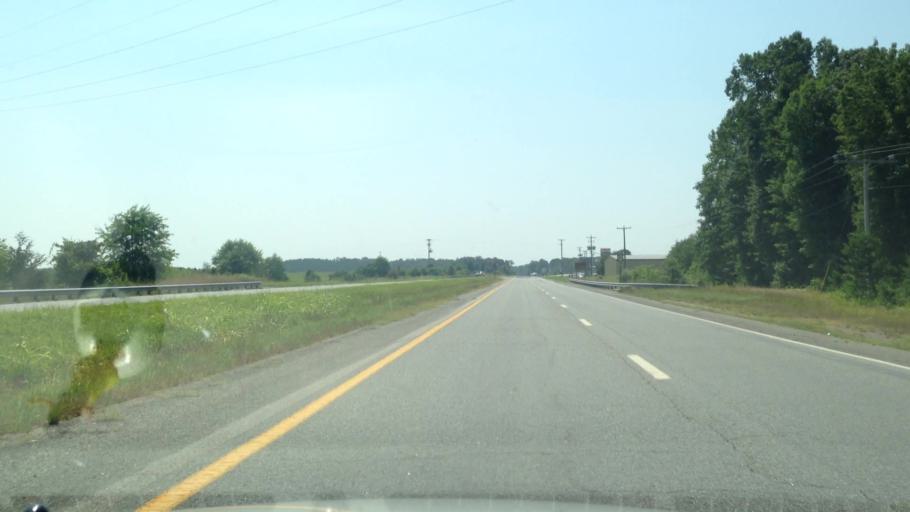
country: US
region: Virginia
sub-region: Patrick County
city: Patrick Springs
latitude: 36.6016
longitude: -80.1608
